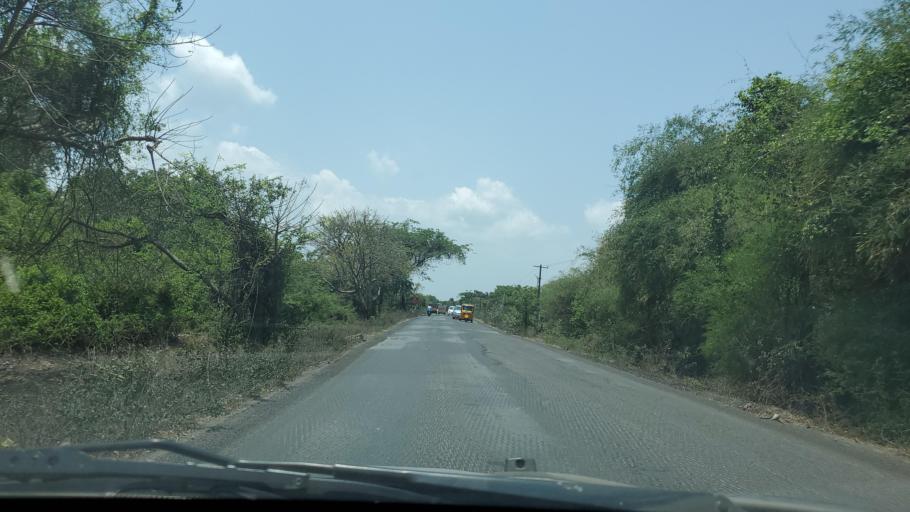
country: IN
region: Tamil Nadu
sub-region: Kancheepuram
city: Vengavasal
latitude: 12.8728
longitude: 80.1729
